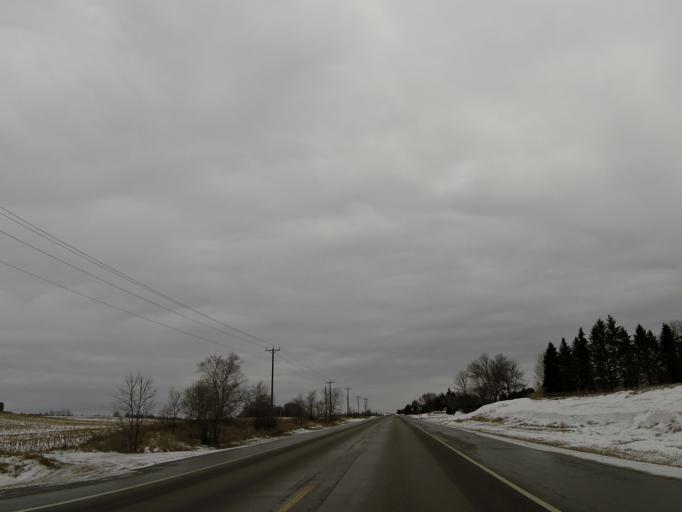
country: US
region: Minnesota
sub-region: Washington County
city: Cottage Grove
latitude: 44.8796
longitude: -92.9033
